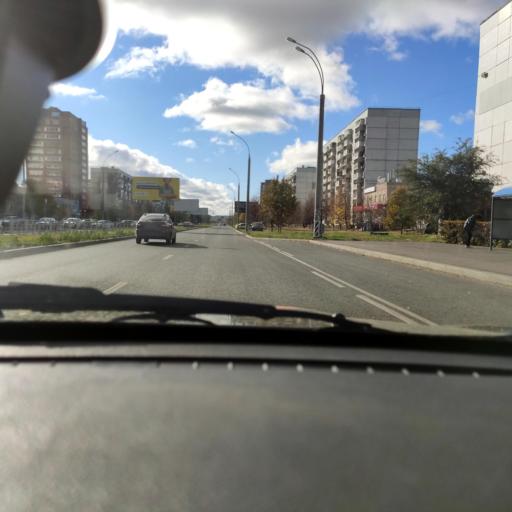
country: RU
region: Samara
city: Tol'yatti
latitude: 53.5471
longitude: 49.3318
